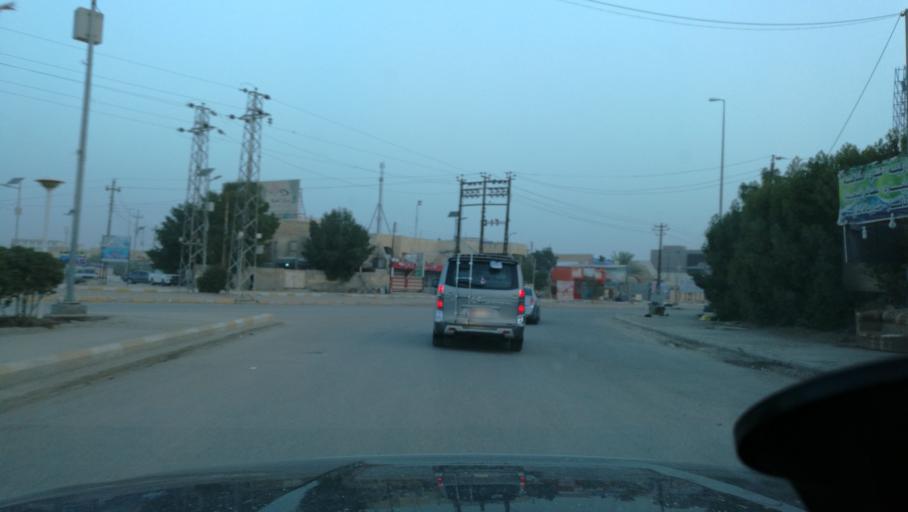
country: IQ
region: Dhi Qar
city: An Nasiriyah
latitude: 31.0318
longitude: 46.2359
